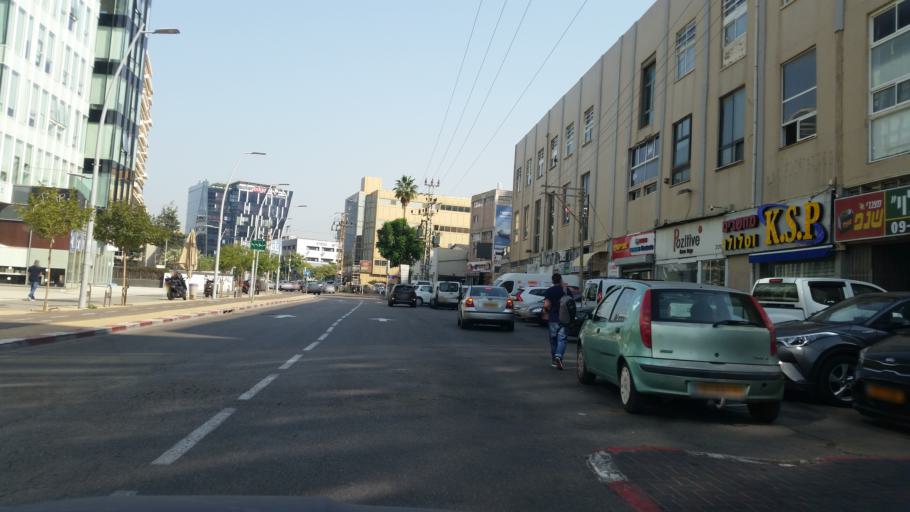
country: IL
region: Tel Aviv
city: Herzliya Pituah
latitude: 32.1644
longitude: 34.8112
